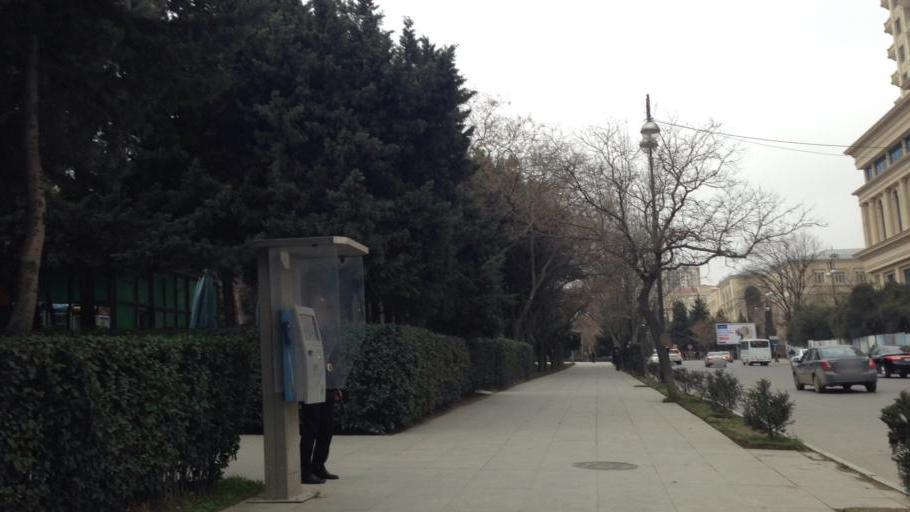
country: AZ
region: Baki
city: Badamdar
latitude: 40.3742
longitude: 49.8178
